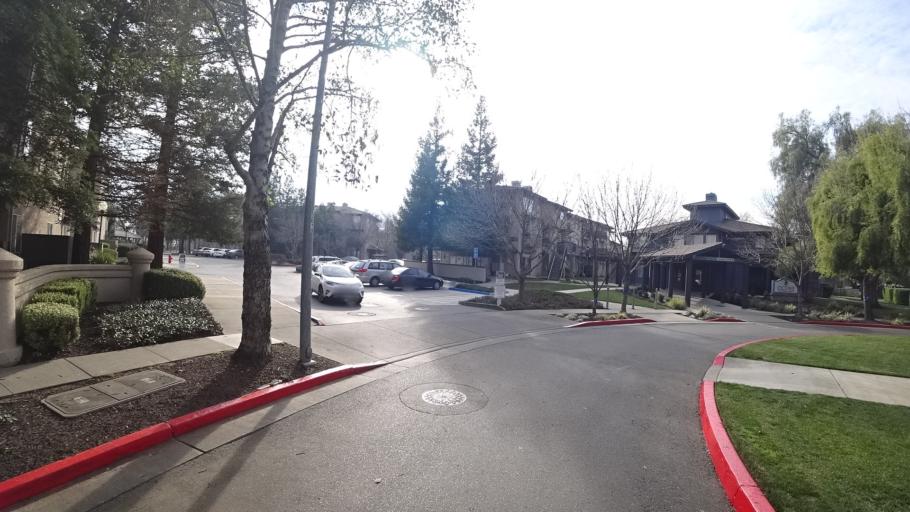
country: US
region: California
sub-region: Yolo County
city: Davis
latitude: 38.5374
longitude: -121.7268
